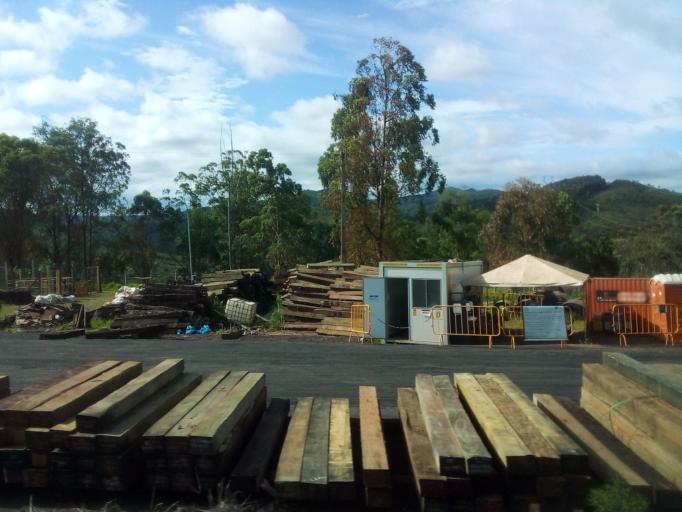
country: BR
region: Minas Gerais
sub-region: Raposos
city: Raposos
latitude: -19.8731
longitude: -43.7777
